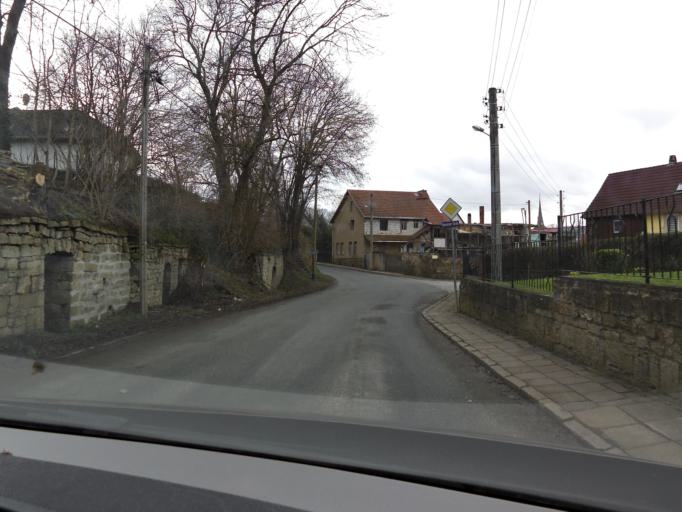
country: DE
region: Thuringia
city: Niederrossla
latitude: 51.0021
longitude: 11.4888
